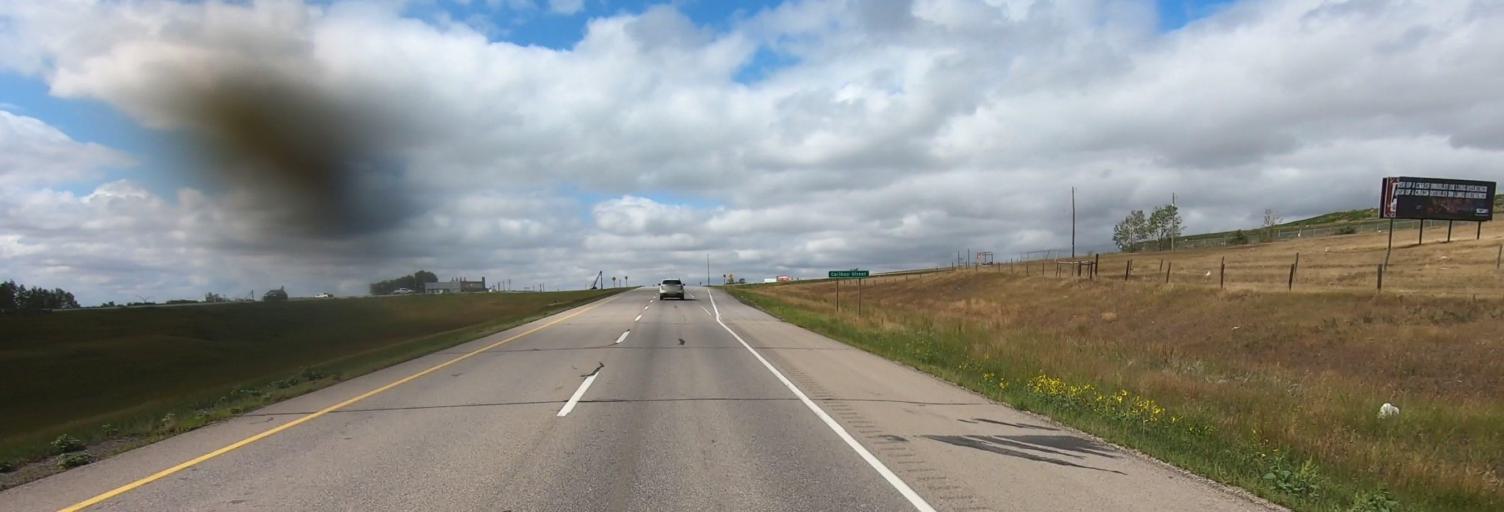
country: CA
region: Saskatchewan
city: Moose Jaw
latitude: 50.3964
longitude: -105.4831
